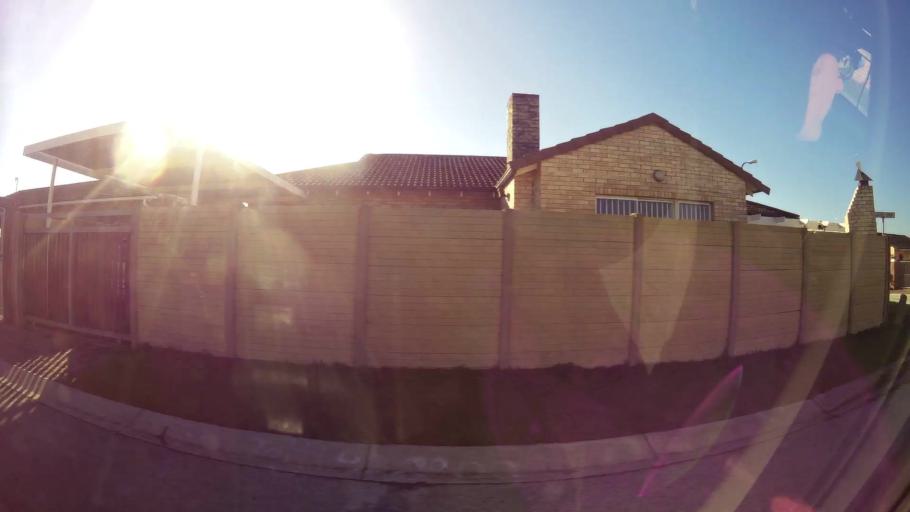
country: ZA
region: Eastern Cape
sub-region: Nelson Mandela Bay Metropolitan Municipality
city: Port Elizabeth
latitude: -33.9778
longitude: 25.6306
